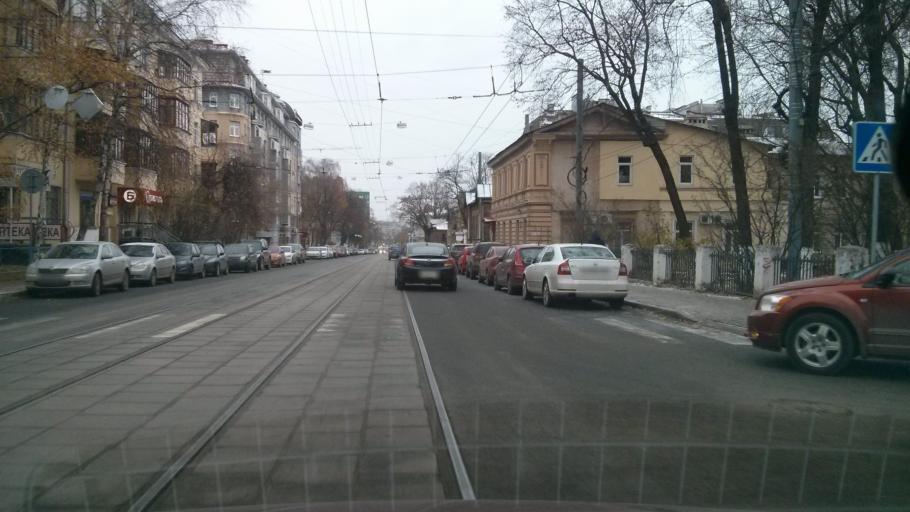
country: RU
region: Nizjnij Novgorod
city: Nizhniy Novgorod
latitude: 56.3246
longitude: 44.0243
